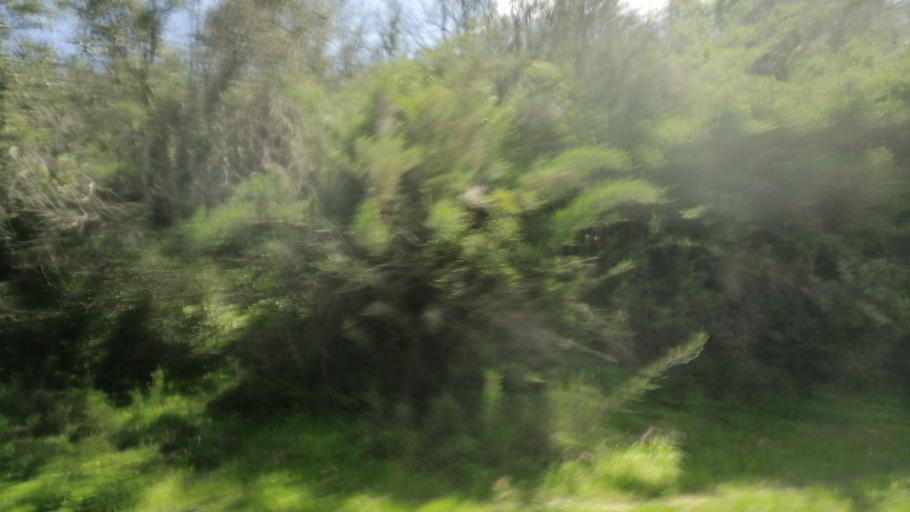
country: CL
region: Valparaiso
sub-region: Provincia de Marga Marga
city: Limache
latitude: -33.1999
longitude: -71.2394
